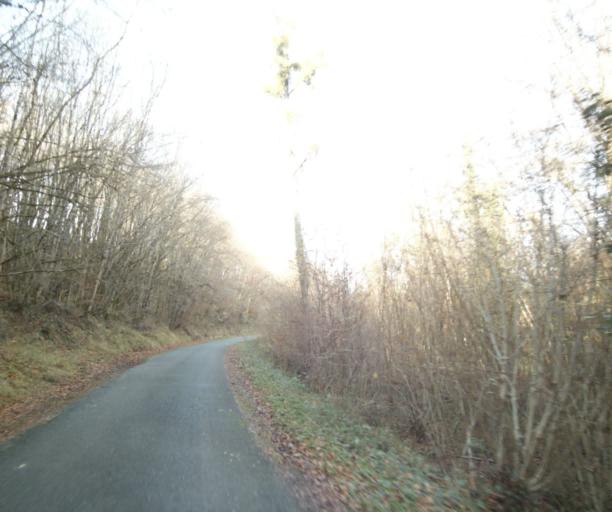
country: FR
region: Poitou-Charentes
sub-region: Departement de la Charente-Maritime
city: Chaniers
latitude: 45.7312
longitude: -0.5386
